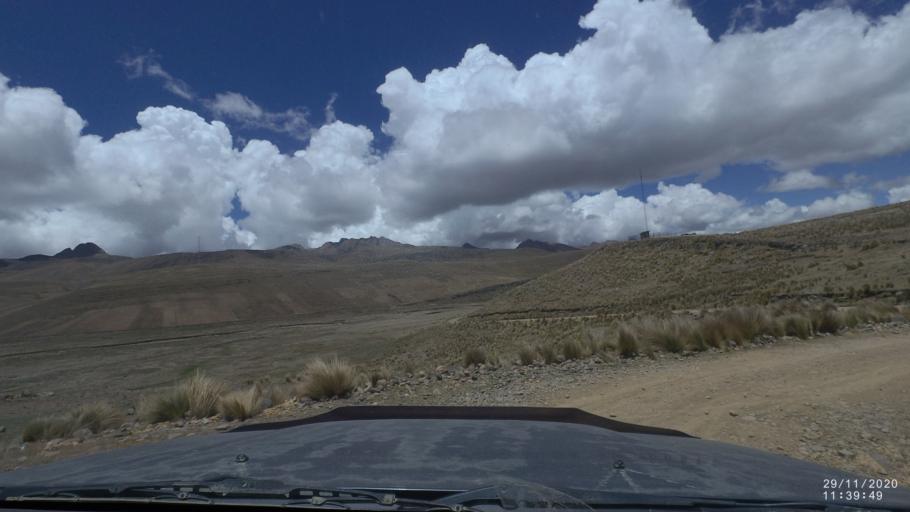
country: BO
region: Cochabamba
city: Cochabamba
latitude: -17.1980
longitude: -66.2403
